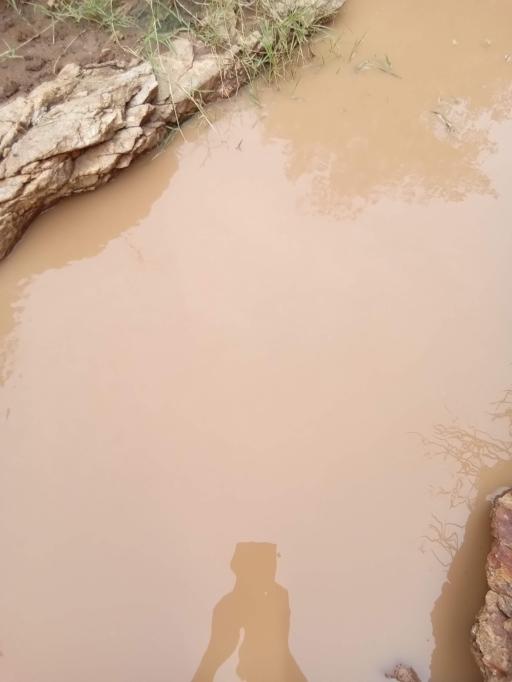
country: KE
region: Homa Bay
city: Homa Bay
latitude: -0.5005
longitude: 34.1636
